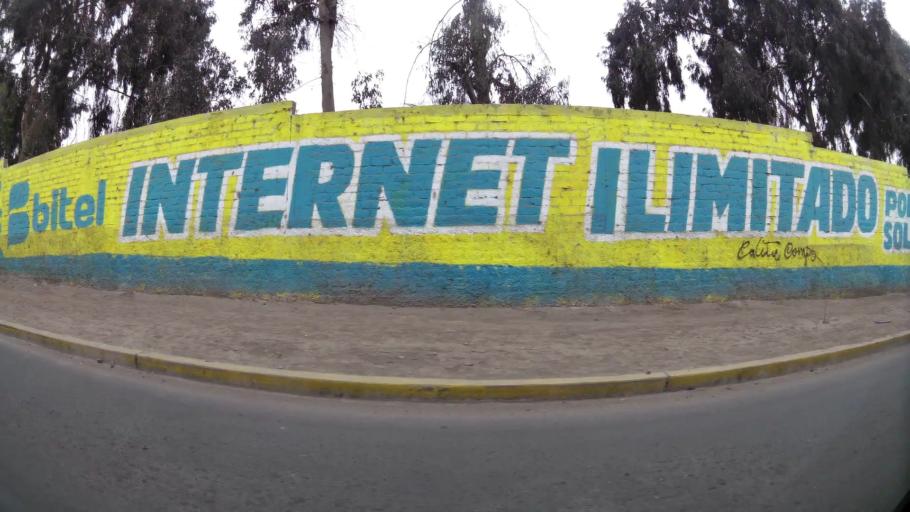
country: PE
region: Lima
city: Ventanilla
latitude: -11.9222
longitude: -77.0810
